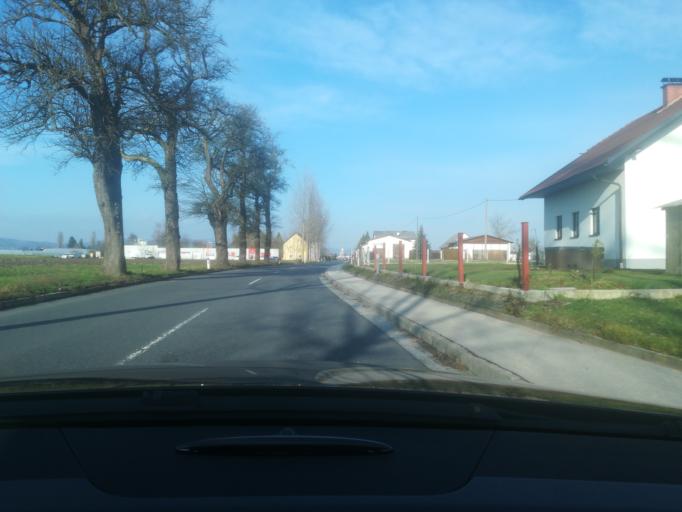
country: AT
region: Upper Austria
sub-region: Politischer Bezirk Urfahr-Umgebung
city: Feldkirchen an der Donau
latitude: 48.2932
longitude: 14.0271
